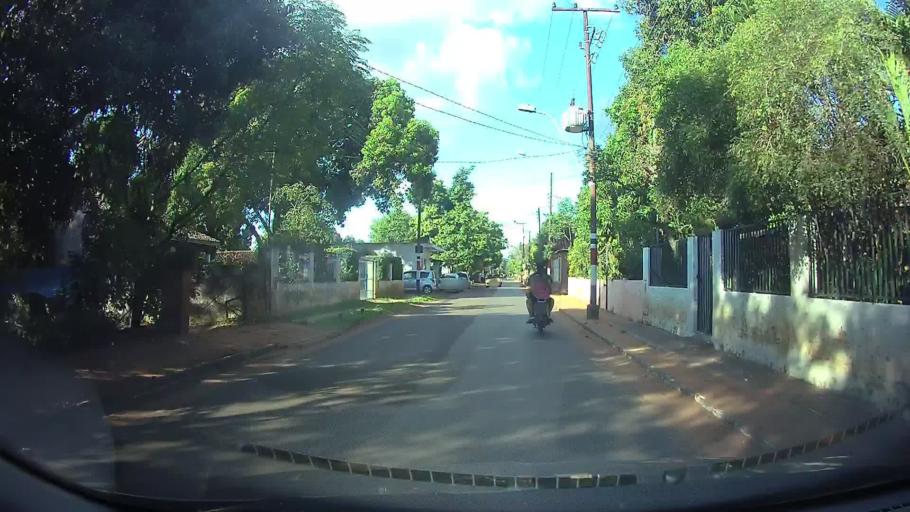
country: PY
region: Central
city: Aregua
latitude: -25.2888
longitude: -57.4398
